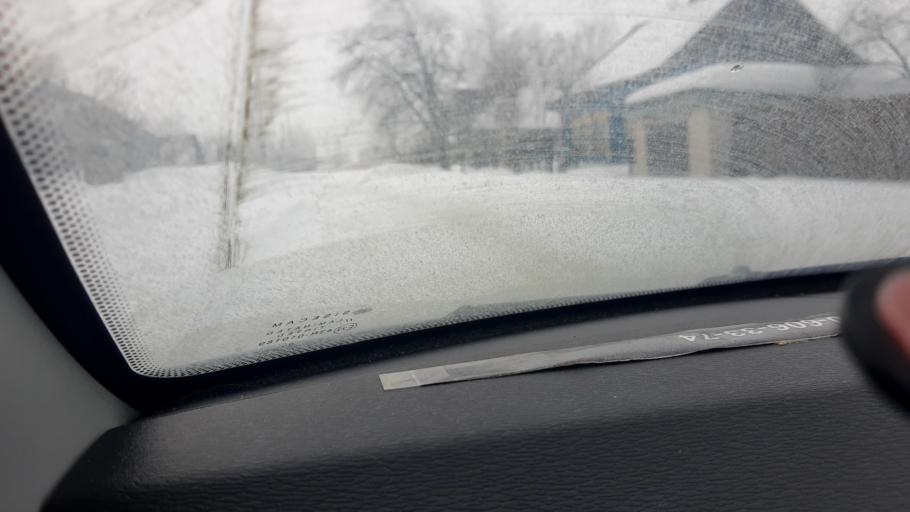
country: RU
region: Nizjnij Novgorod
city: Sitniki
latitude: 56.5280
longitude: 44.0557
